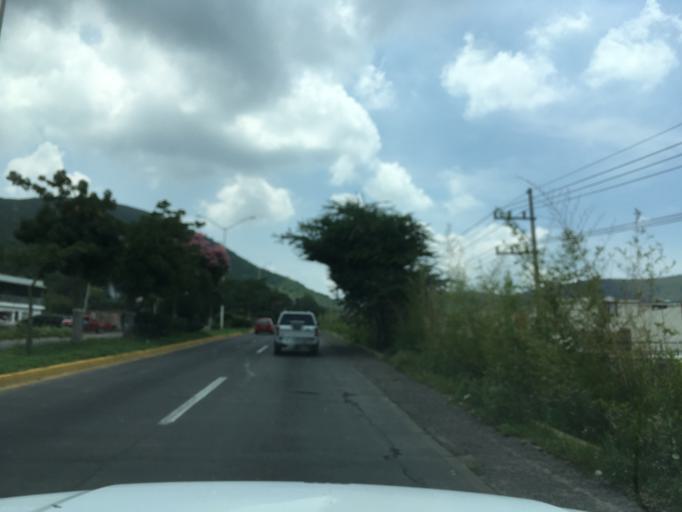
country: MX
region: Jalisco
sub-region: Tlajomulco de Zuniga
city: Santa Cruz de las Flores
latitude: 20.4906
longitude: -103.4776
